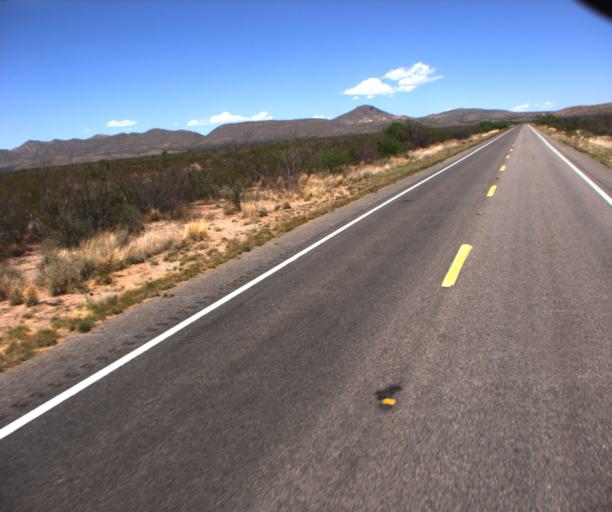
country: US
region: Arizona
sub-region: Cochise County
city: Tombstone
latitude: 31.6221
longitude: -110.0505
